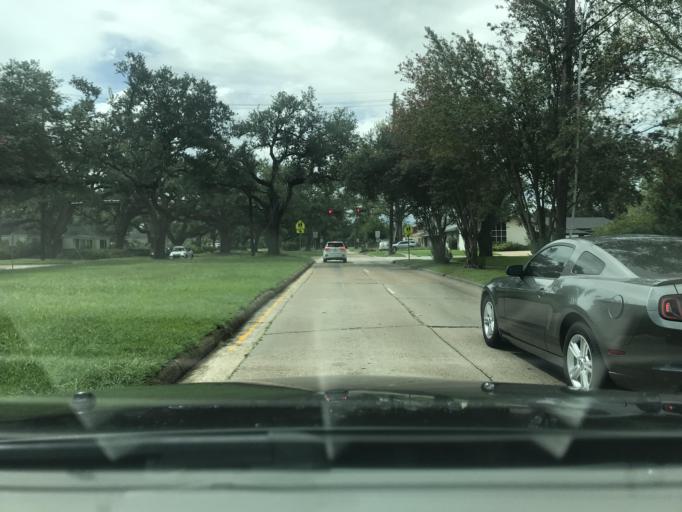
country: US
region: Louisiana
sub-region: Calcasieu Parish
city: Lake Charles
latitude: 30.2195
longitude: -93.2044
